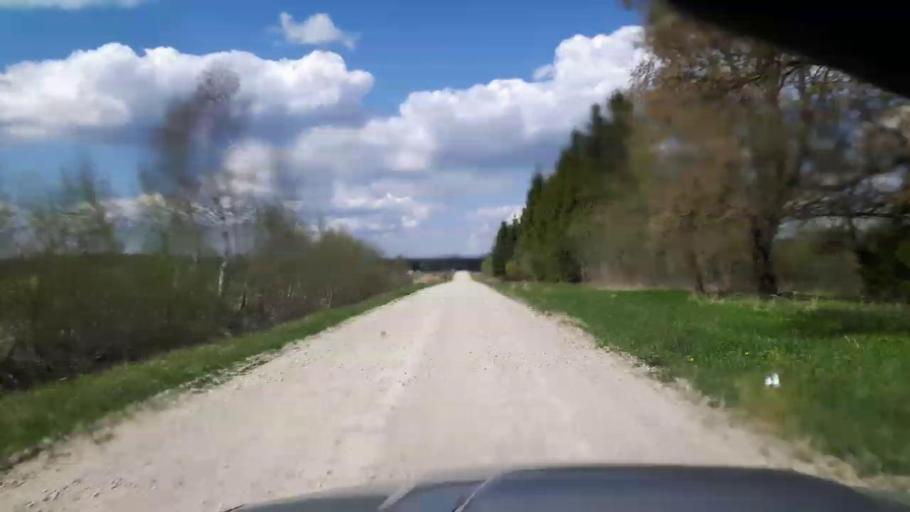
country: EE
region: Paernumaa
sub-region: Tootsi vald
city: Tootsi
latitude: 58.4605
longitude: 24.8758
